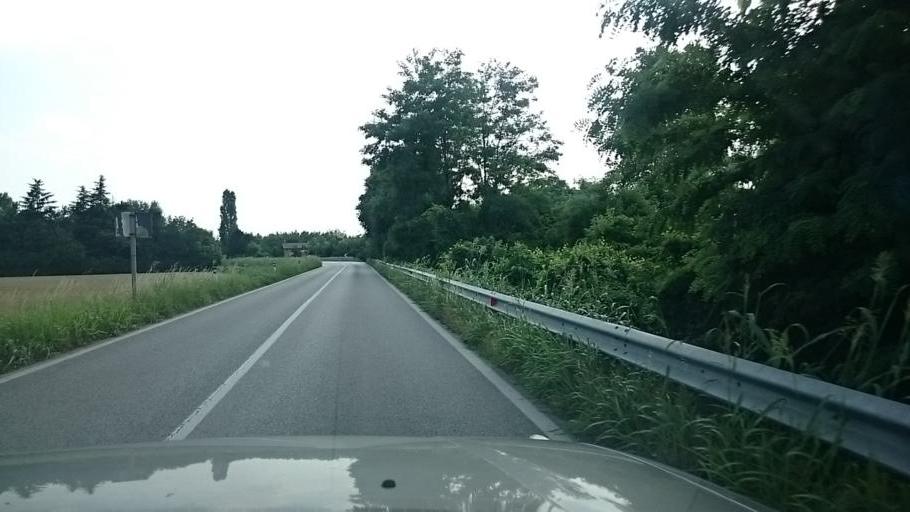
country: IT
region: Veneto
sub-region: Provincia di Padova
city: Santa Maria di Non
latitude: 45.5114
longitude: 11.8632
